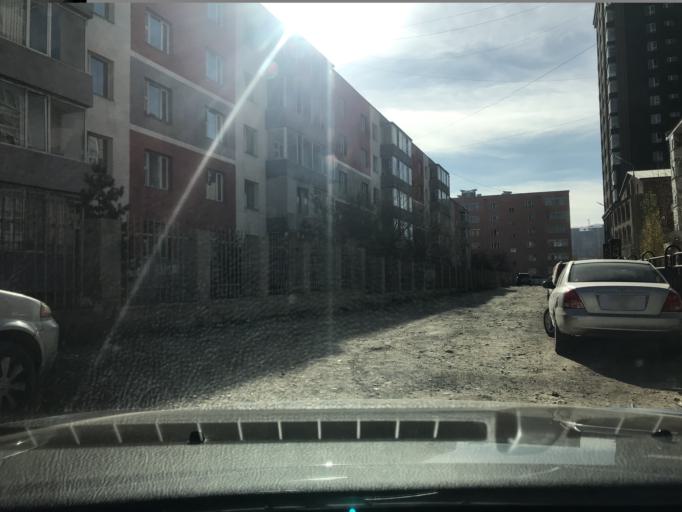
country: MN
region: Ulaanbaatar
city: Ulaanbaatar
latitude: 47.9100
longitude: 106.9400
